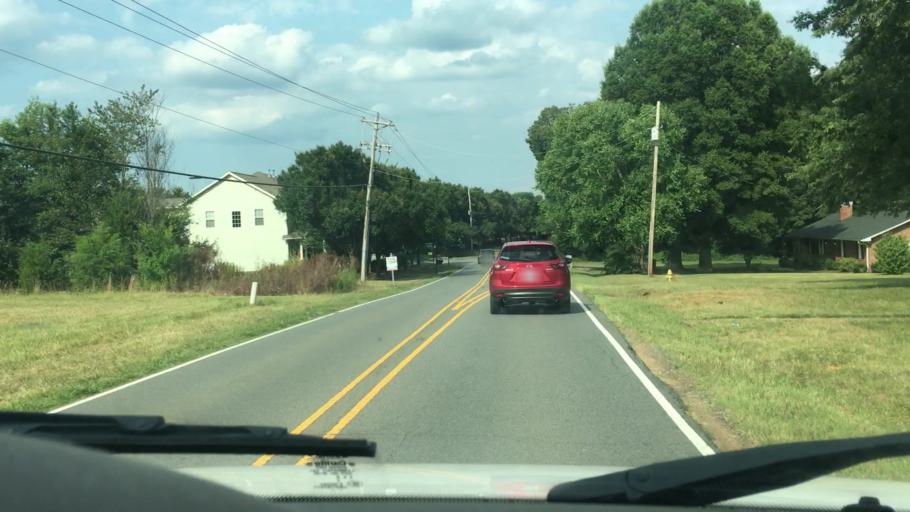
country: US
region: North Carolina
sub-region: Mecklenburg County
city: Huntersville
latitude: 35.4253
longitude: -80.8501
